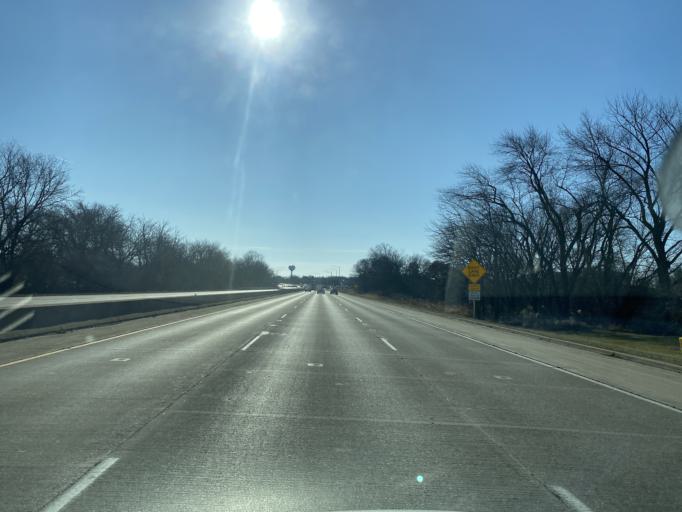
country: US
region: Illinois
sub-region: DuPage County
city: Willowbrook
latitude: 41.7788
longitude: -87.9469
